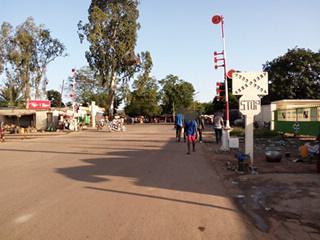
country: CI
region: Vallee du Bandama
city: Bouake
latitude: 7.6879
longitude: -5.0261
